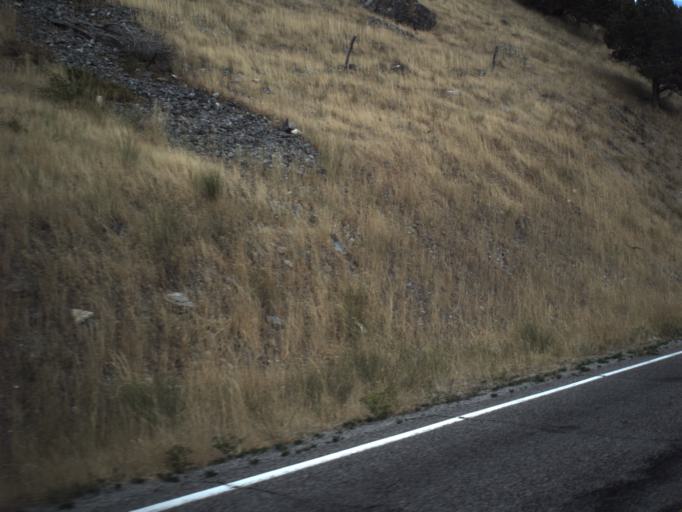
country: US
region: Utah
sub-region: Cache County
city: Hyrum
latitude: 41.6259
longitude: -111.7969
